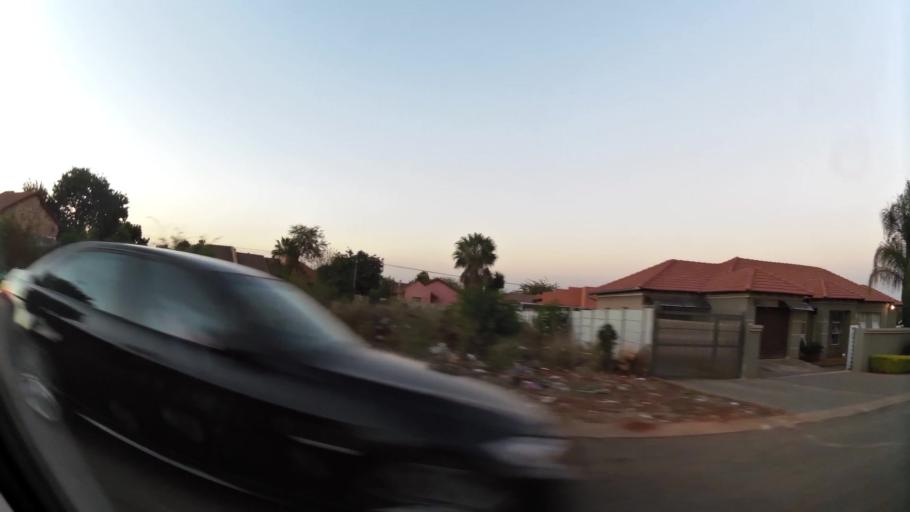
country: ZA
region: North-West
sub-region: Bojanala Platinum District Municipality
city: Rustenburg
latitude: -25.6590
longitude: 27.2109
